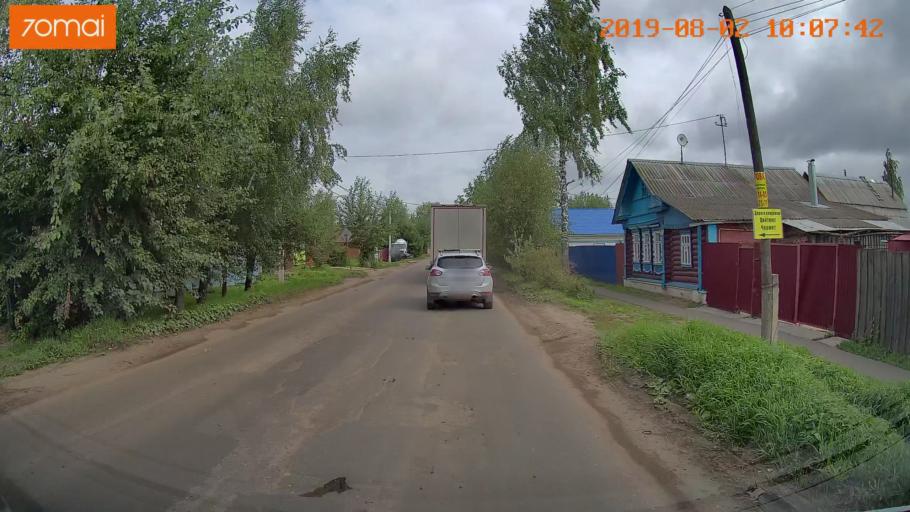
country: RU
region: Ivanovo
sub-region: Gorod Ivanovo
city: Ivanovo
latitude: 56.9833
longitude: 40.9363
